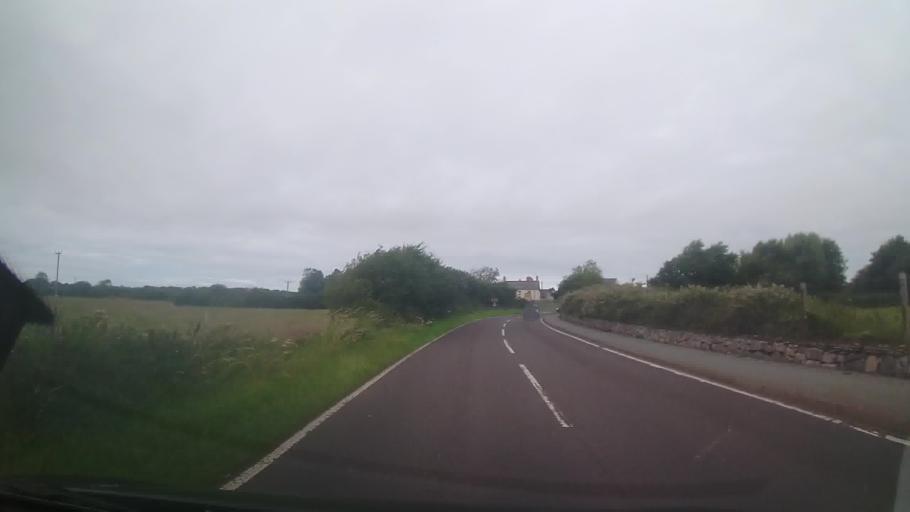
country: GB
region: Wales
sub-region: Gwynedd
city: Caernarfon
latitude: 53.1624
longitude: -4.3538
